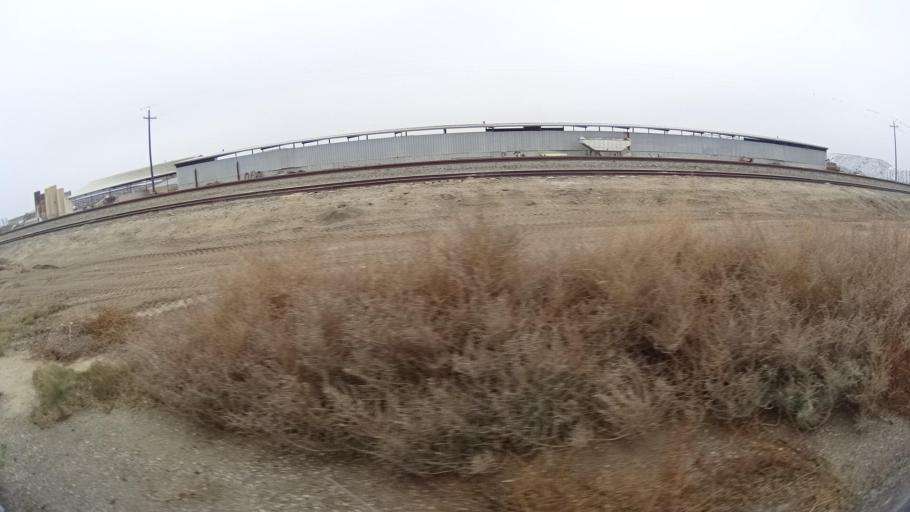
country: US
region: California
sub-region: Kern County
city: Greenfield
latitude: 35.1802
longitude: -119.1207
